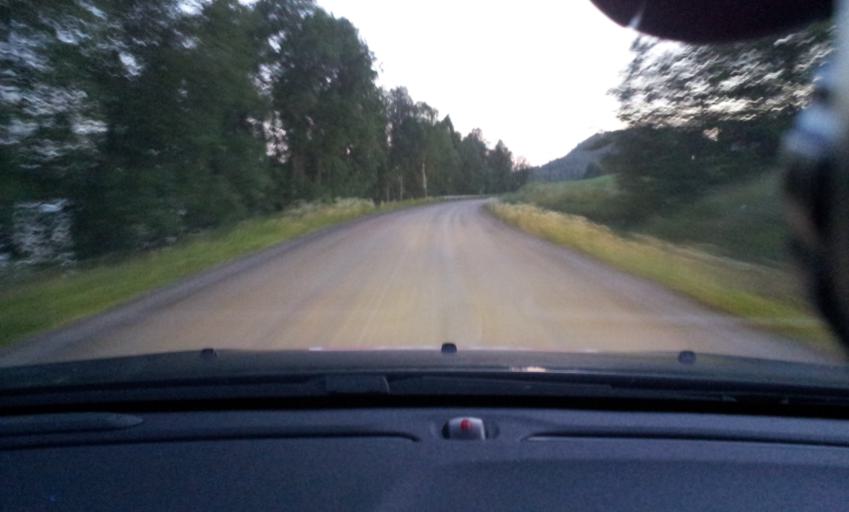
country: SE
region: Jaemtland
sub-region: Braecke Kommun
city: Braecke
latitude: 62.7172
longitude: 15.5958
